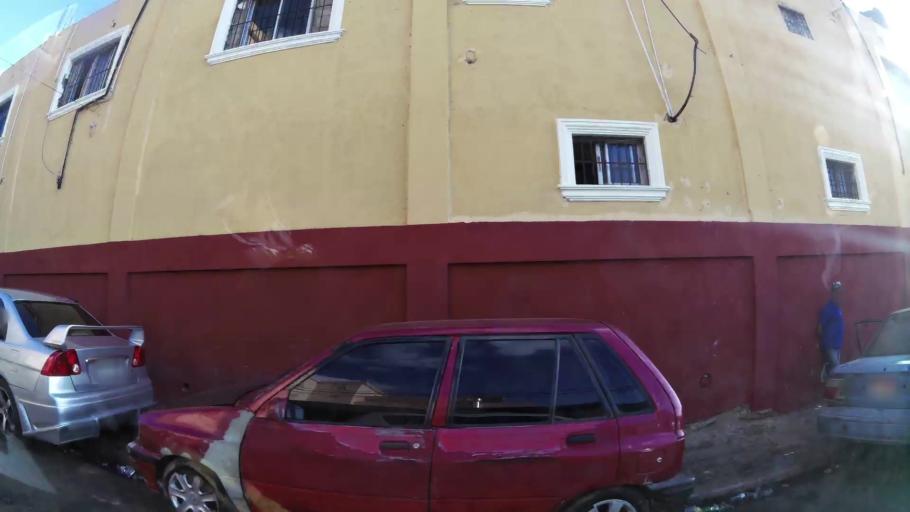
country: DO
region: Nacional
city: Ensanche Luperon
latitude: 18.5439
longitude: -69.9010
